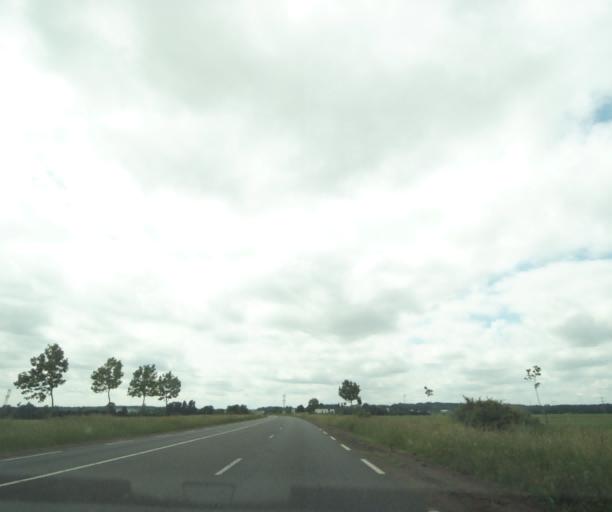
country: FR
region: Poitou-Charentes
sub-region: Departement des Deux-Sevres
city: Saint-Varent
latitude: 46.8389
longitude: -0.2083
